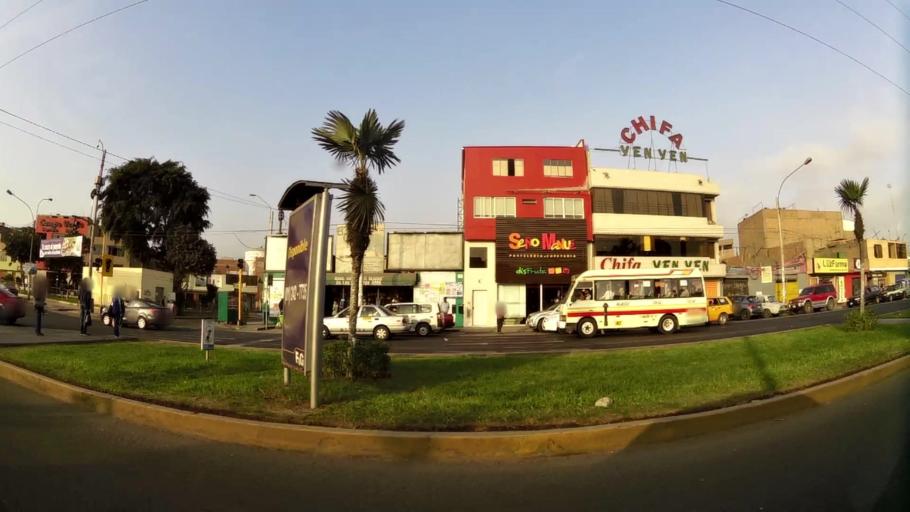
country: PE
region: Lima
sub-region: Lima
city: Independencia
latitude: -11.9870
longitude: -77.0723
